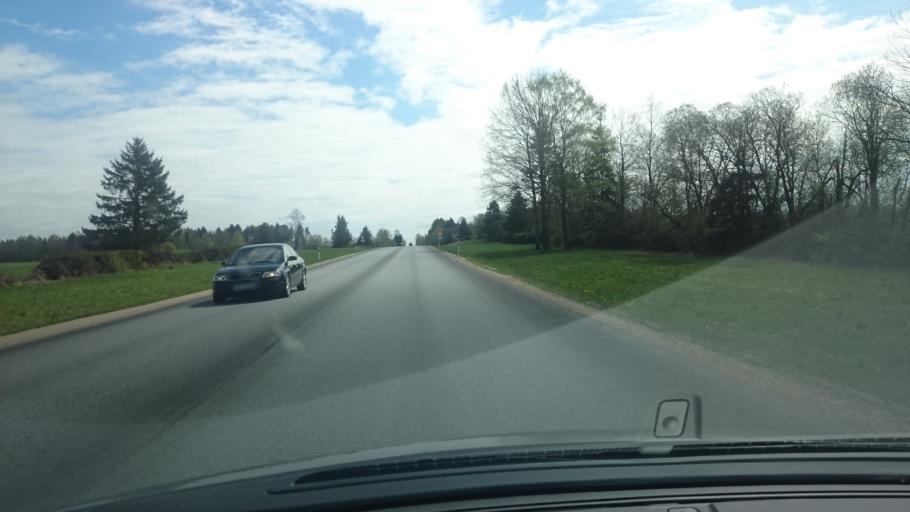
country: EE
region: Laeaene-Virumaa
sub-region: Kadrina vald
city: Kadrina
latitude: 59.4384
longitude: 26.1395
